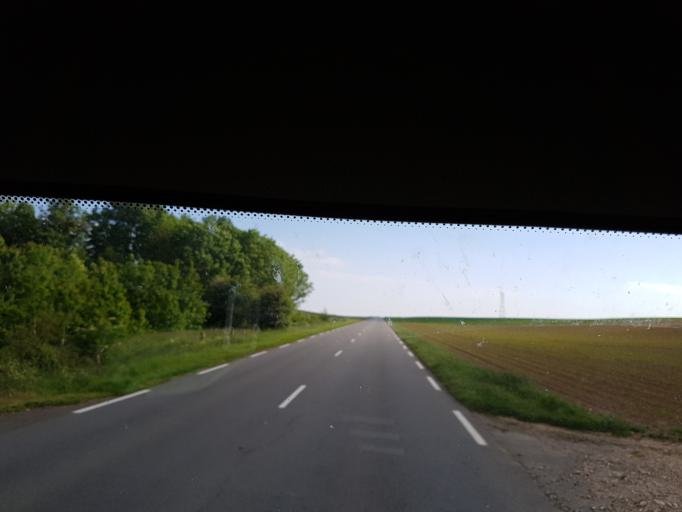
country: FR
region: Picardie
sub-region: Departement de la Somme
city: Crecy-en-Ponthieu
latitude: 50.2524
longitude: 1.9654
